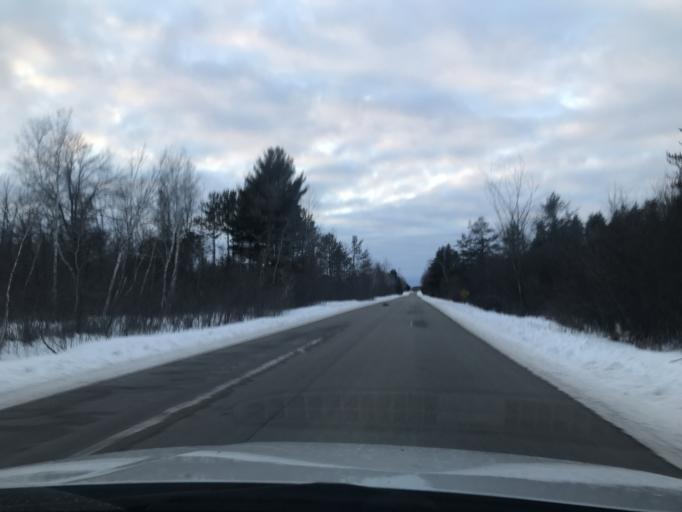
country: US
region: Wisconsin
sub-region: Marinette County
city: Peshtigo
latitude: 45.1646
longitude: -87.7452
